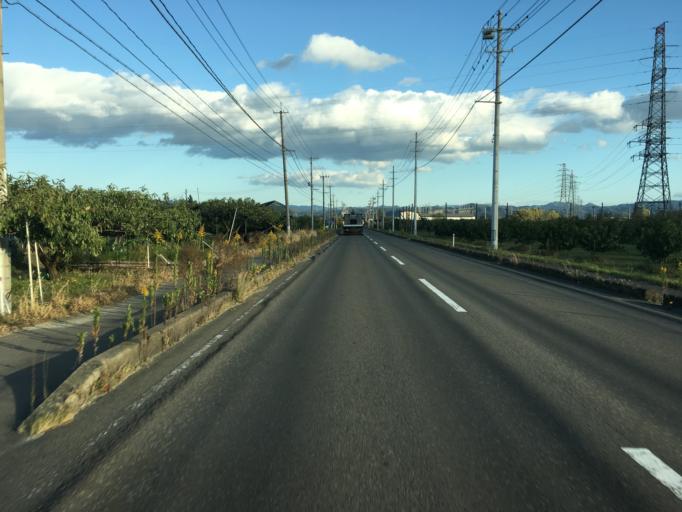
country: JP
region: Fukushima
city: Fukushima-shi
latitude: 37.8169
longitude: 140.4568
